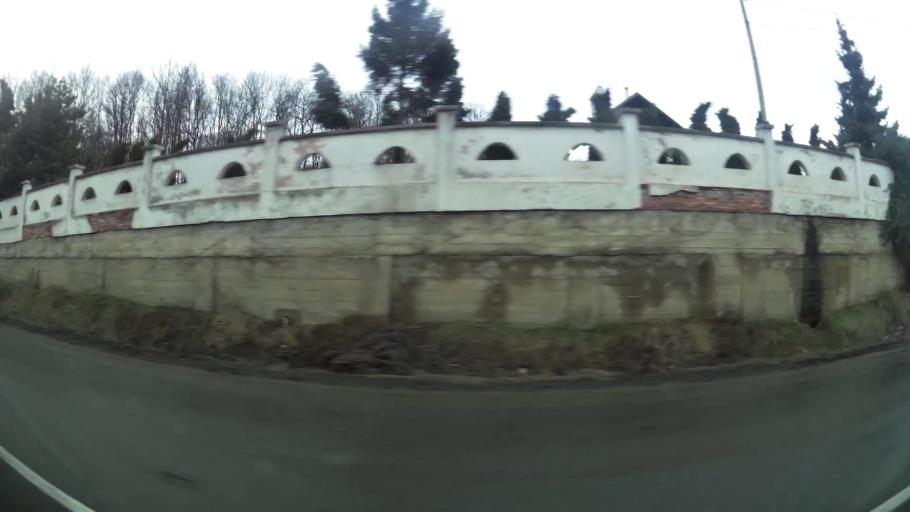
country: RS
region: Central Serbia
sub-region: Belgrade
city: Rakovica
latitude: 44.7265
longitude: 20.4905
